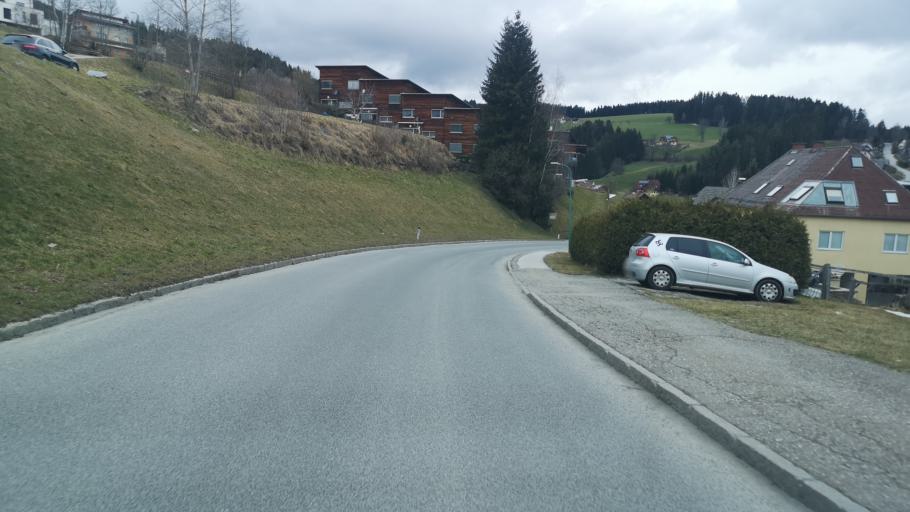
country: AT
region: Styria
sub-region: Politischer Bezirk Weiz
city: Birkfeld
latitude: 47.3561
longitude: 15.6921
